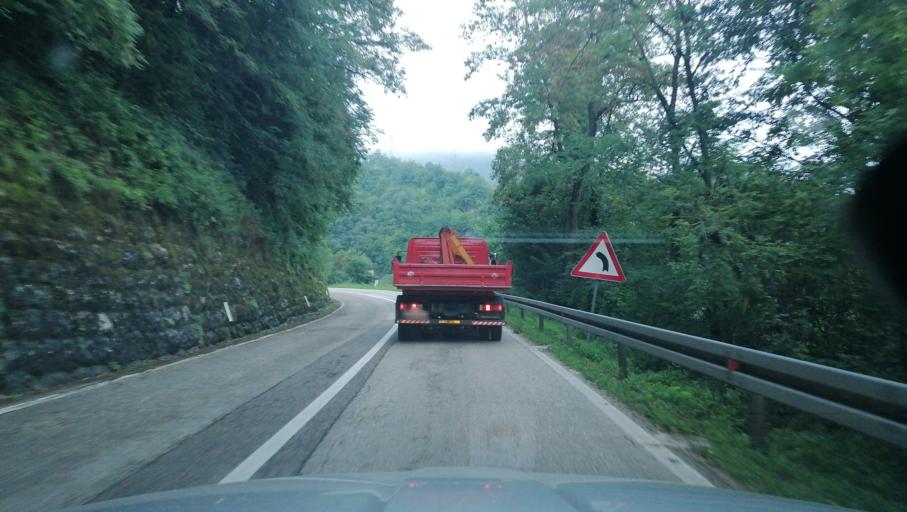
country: BA
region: Federation of Bosnia and Herzegovina
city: Jablanica
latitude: 43.7275
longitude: 17.6894
